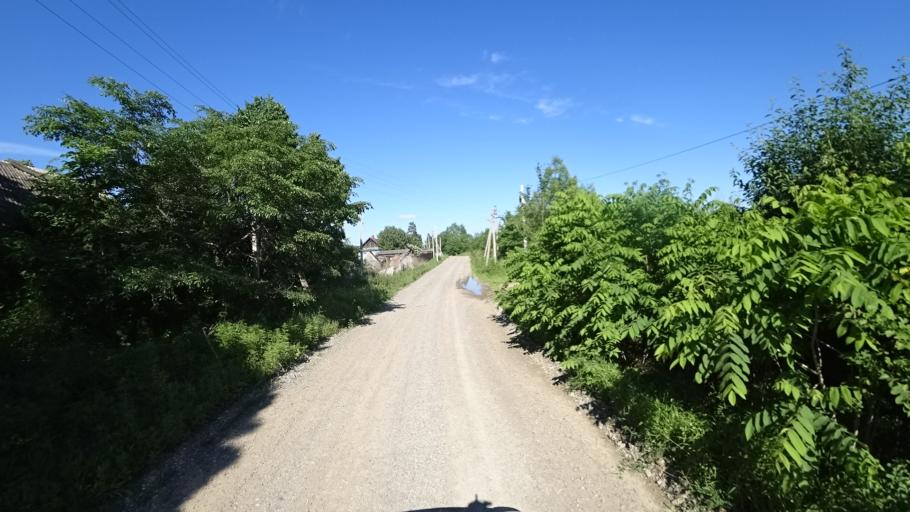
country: RU
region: Khabarovsk Krai
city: Khor
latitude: 47.8864
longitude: 135.0082
